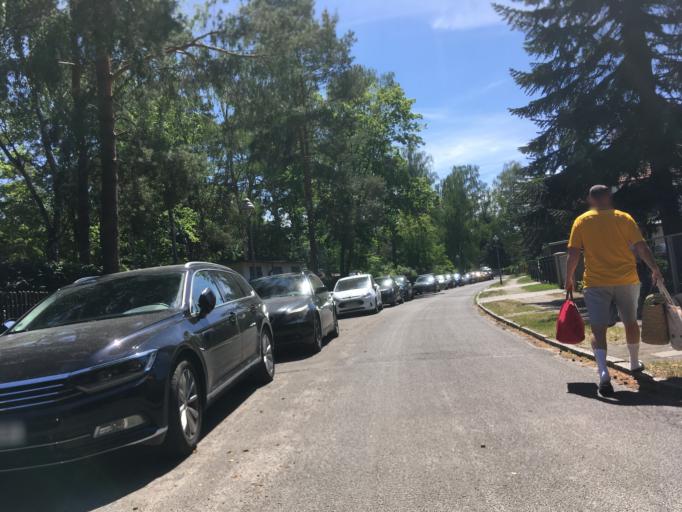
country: DE
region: Berlin
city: Schmockwitz
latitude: 52.3895
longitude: 13.6408
